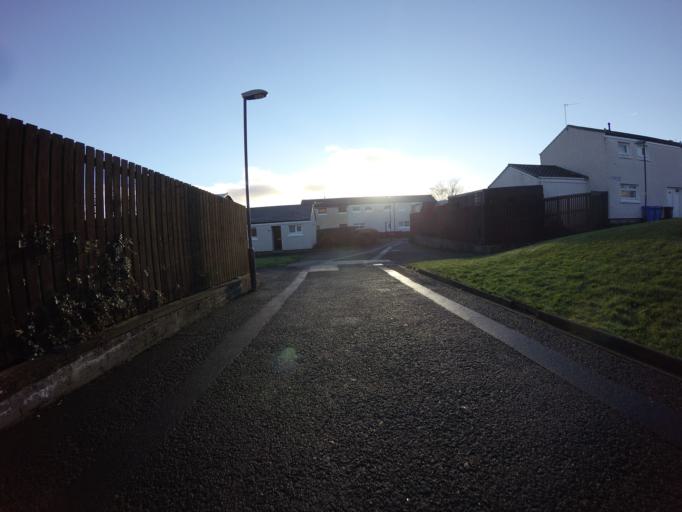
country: GB
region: Scotland
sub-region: West Lothian
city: Livingston
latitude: 55.8943
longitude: -3.5107
